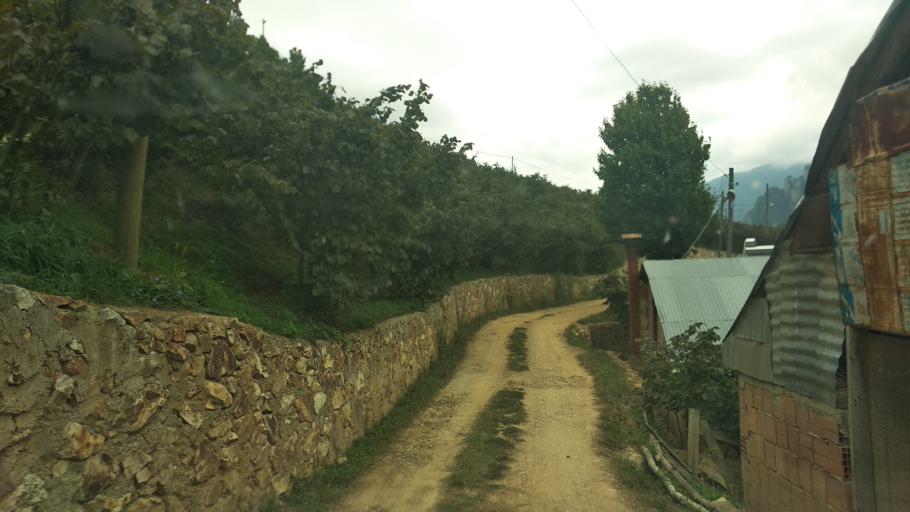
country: TR
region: Giresun
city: Dogankent
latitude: 40.7431
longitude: 38.9958
